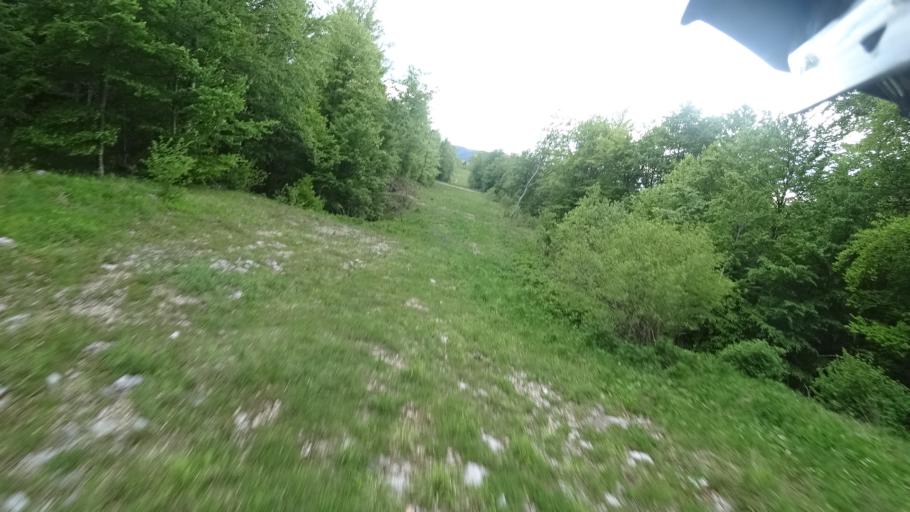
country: HR
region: Karlovacka
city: Plaski
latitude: 44.9065
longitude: 15.4169
